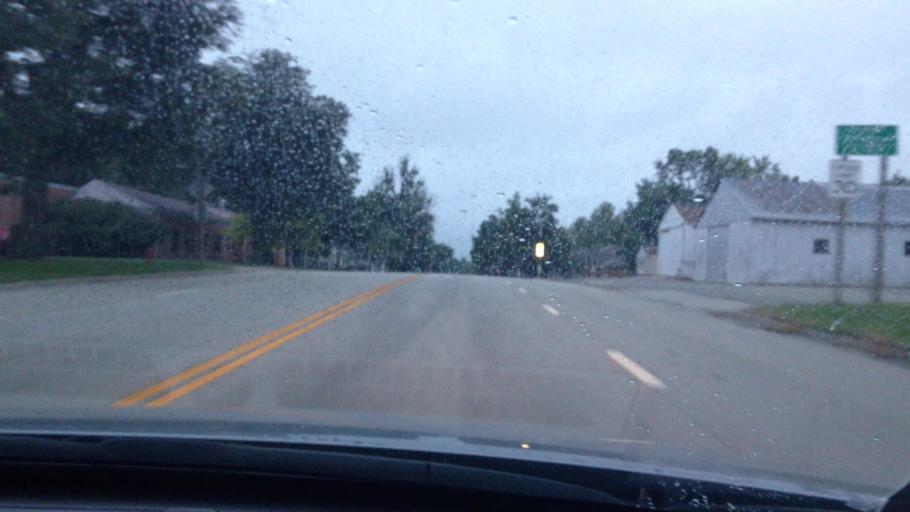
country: US
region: Kansas
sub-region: Brown County
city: Horton
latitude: 39.6719
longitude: -95.5273
